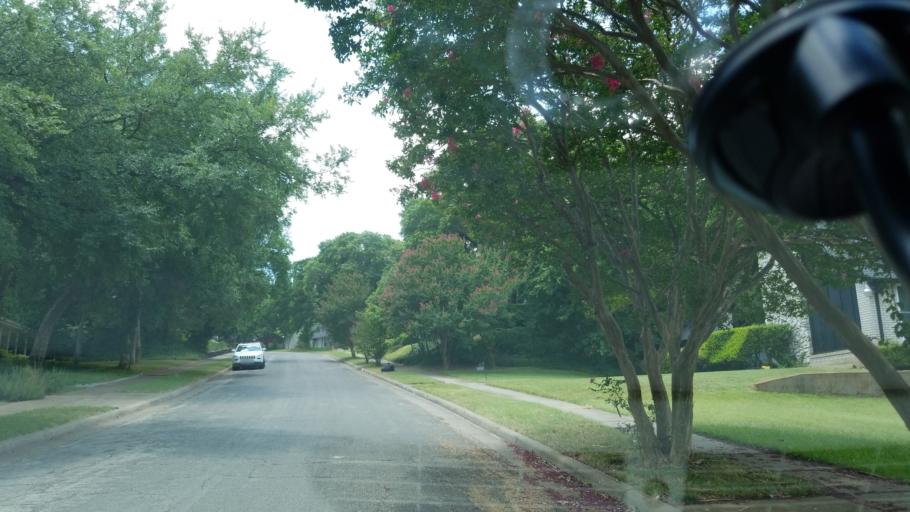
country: US
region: Texas
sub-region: Dallas County
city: Cockrell Hill
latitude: 32.6986
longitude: -96.8486
